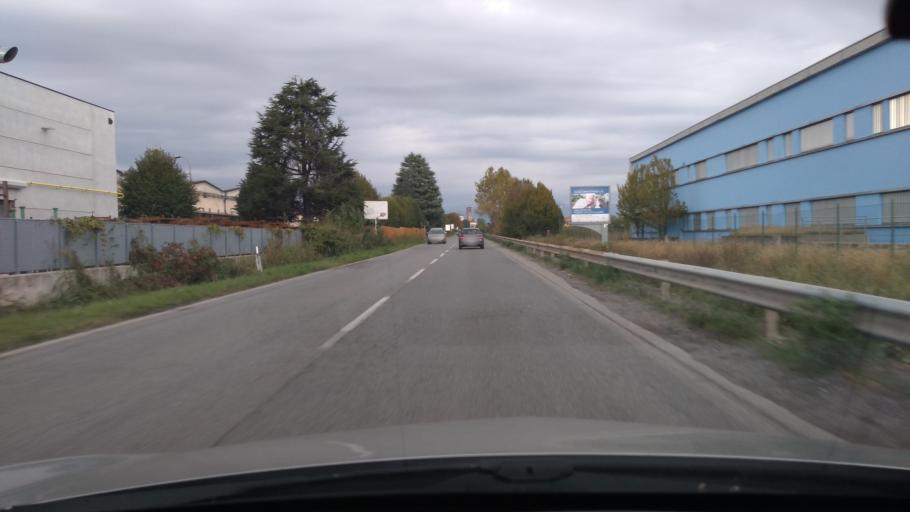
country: IT
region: Lombardy
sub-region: Provincia di Bergamo
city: Verdello
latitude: 45.5955
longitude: 9.6225
